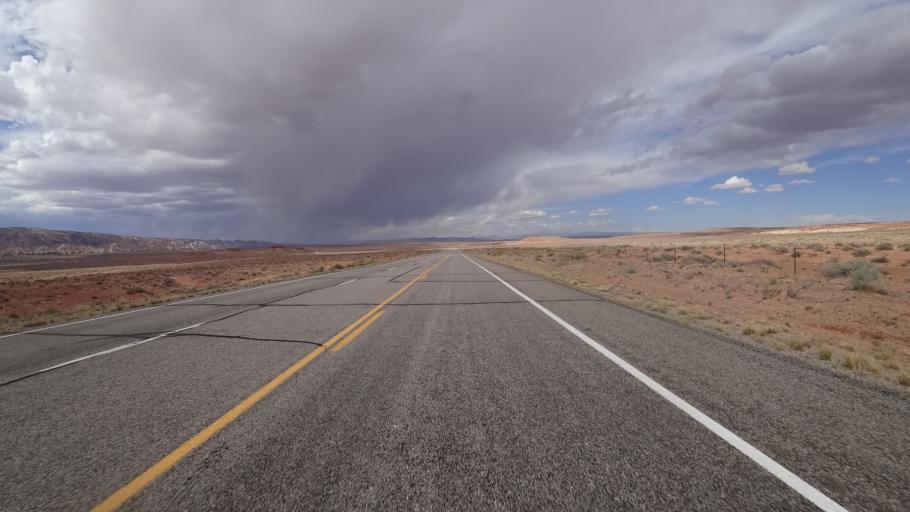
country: US
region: Utah
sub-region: Emery County
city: Castle Dale
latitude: 38.7586
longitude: -110.4493
